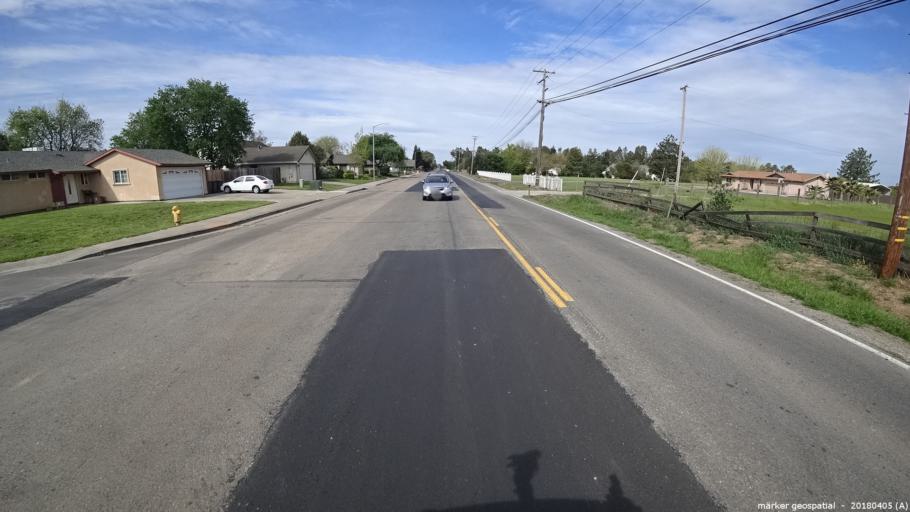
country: US
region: California
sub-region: Sacramento County
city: Galt
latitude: 38.2620
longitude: -121.3123
